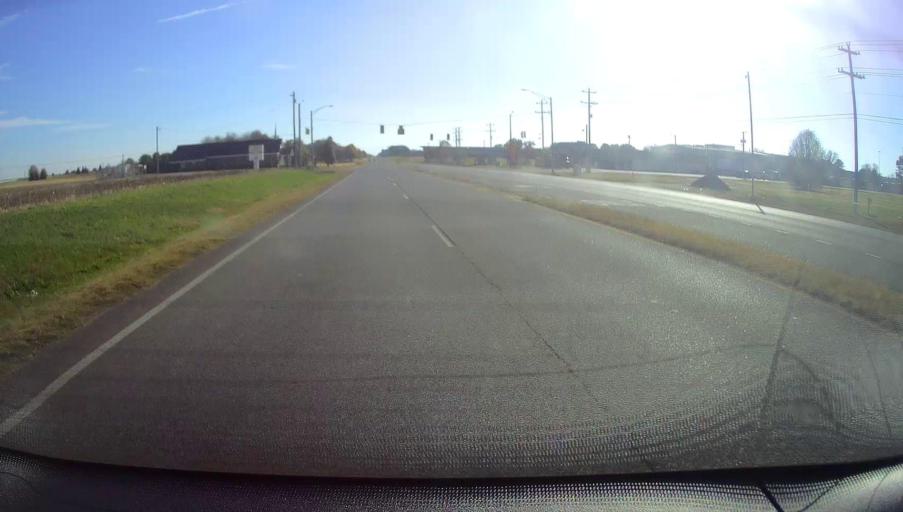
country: US
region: Alabama
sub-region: Morgan County
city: Decatur
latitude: 34.6591
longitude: -86.9502
